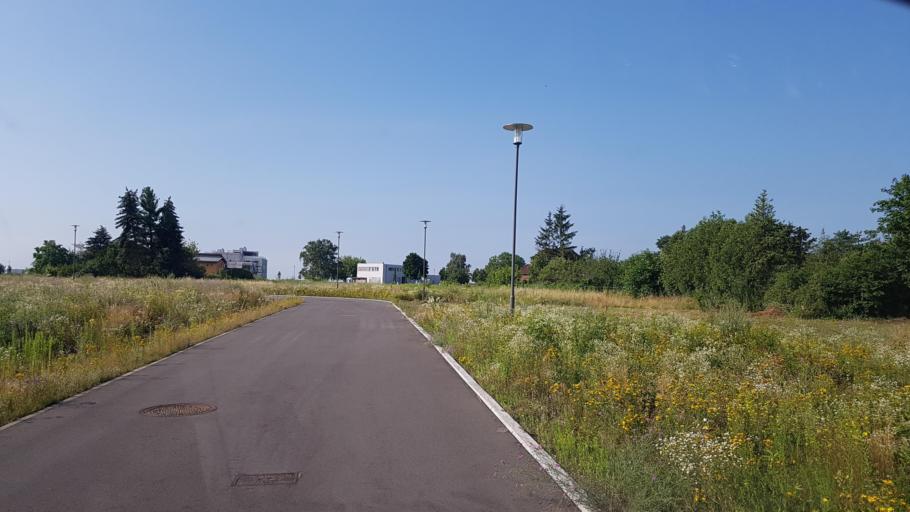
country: DE
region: Brandenburg
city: Grossraschen
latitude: 51.5784
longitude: 14.0133
